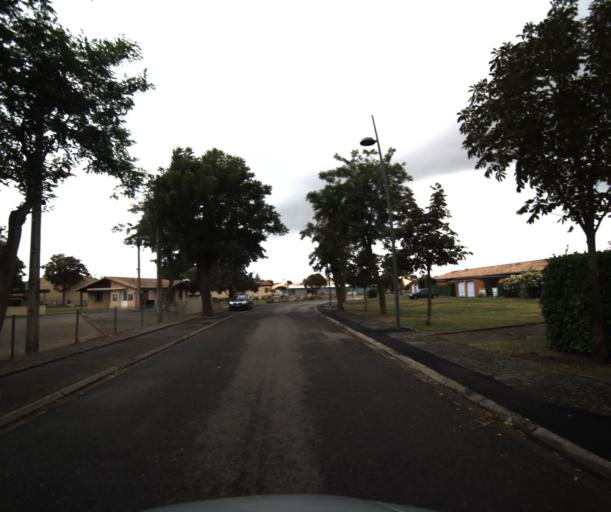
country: FR
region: Midi-Pyrenees
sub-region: Departement de la Haute-Garonne
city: Portet-sur-Garonne
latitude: 43.5405
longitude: 1.4084
